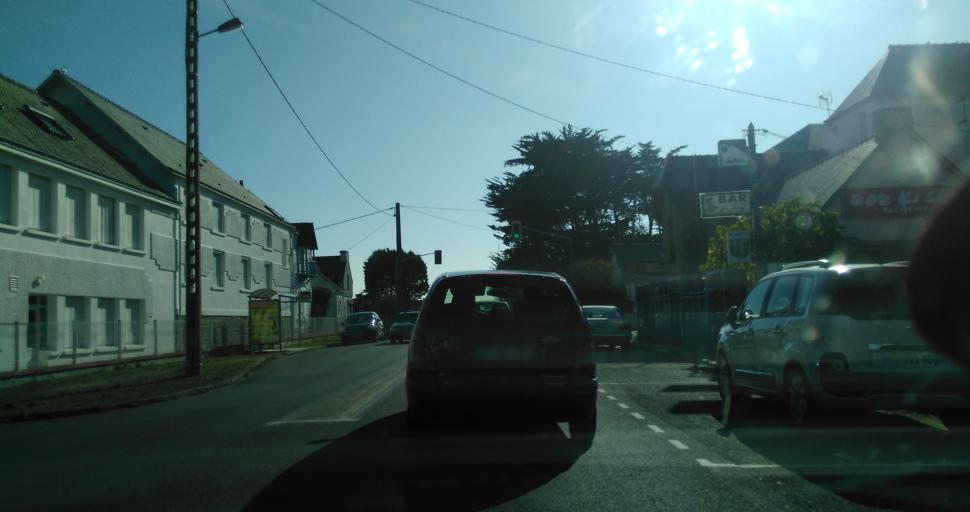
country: FR
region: Brittany
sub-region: Departement du Morbihan
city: Saint-Pierre-Quiberon
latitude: 47.5581
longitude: -3.1344
